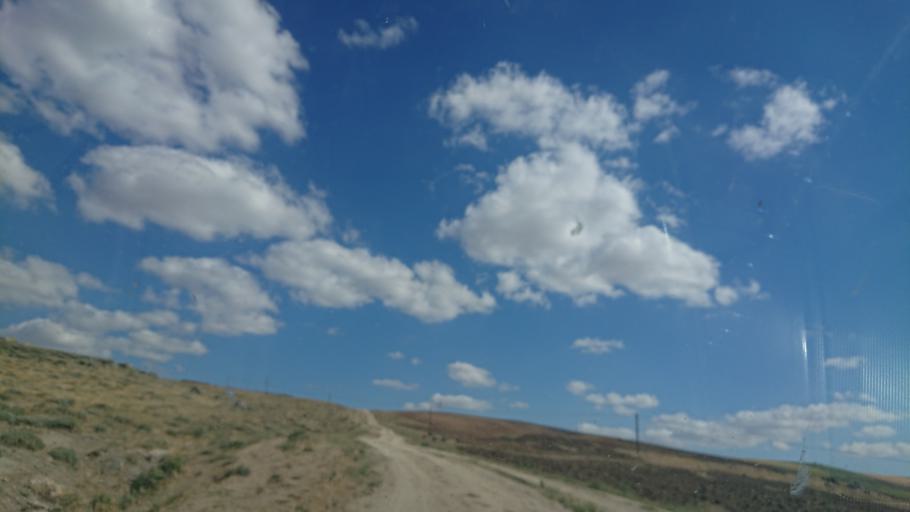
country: TR
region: Aksaray
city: Agacoren
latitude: 38.9125
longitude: 33.8555
